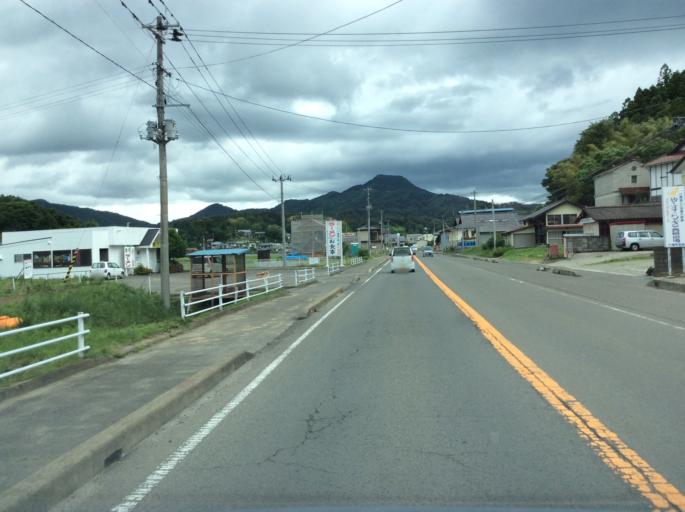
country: JP
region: Fukushima
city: Fukushima-shi
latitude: 37.6767
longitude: 140.5648
